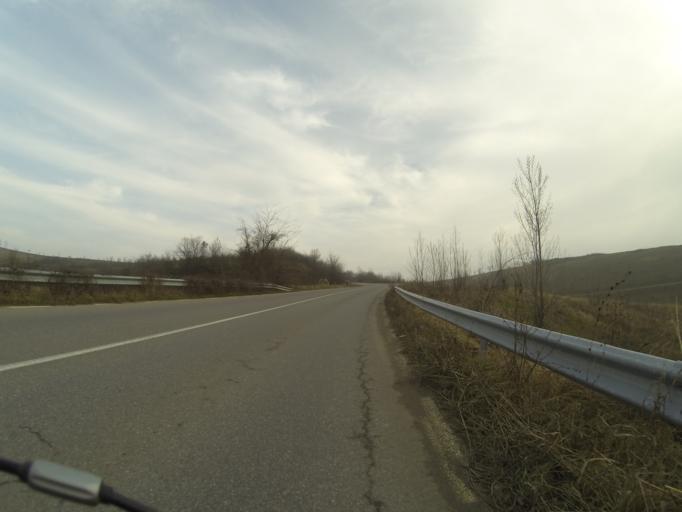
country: RO
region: Mehedinti
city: Vanju-Mare
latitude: 44.4121
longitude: 22.8829
